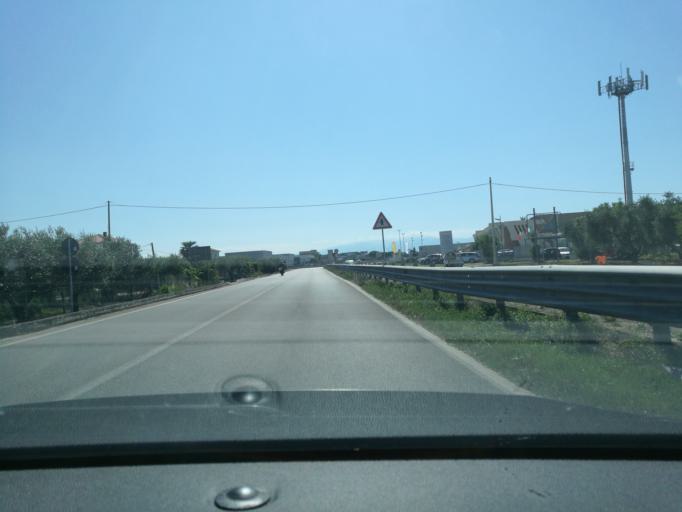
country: IT
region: Abruzzo
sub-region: Provincia di Chieti
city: Vasto
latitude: 42.1675
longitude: 14.6939
